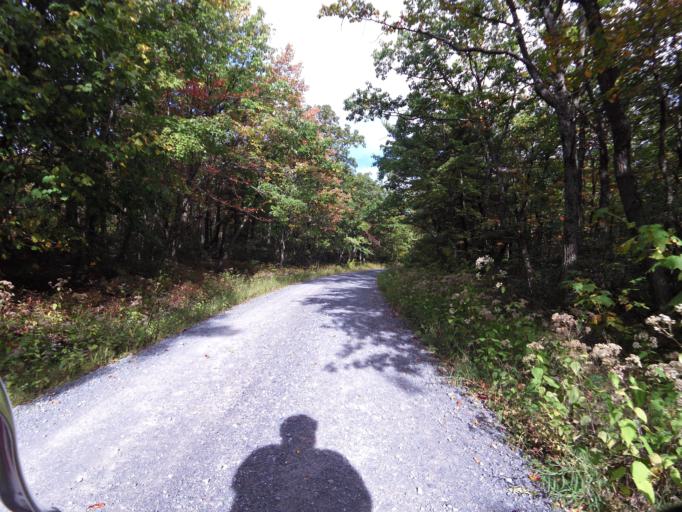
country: US
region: Pennsylvania
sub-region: Lycoming County
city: Jersey Shore
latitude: 41.1104
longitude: -77.1481
